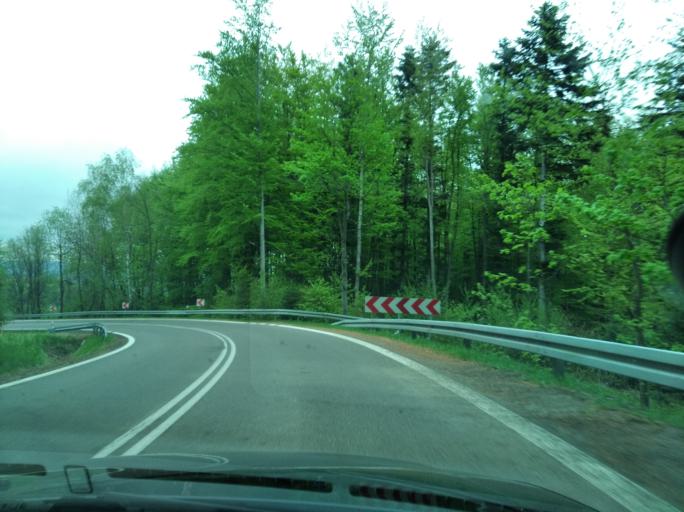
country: PL
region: Subcarpathian Voivodeship
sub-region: Powiat sanocki
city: Tyrawa Woloska
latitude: 49.5640
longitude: 22.3429
